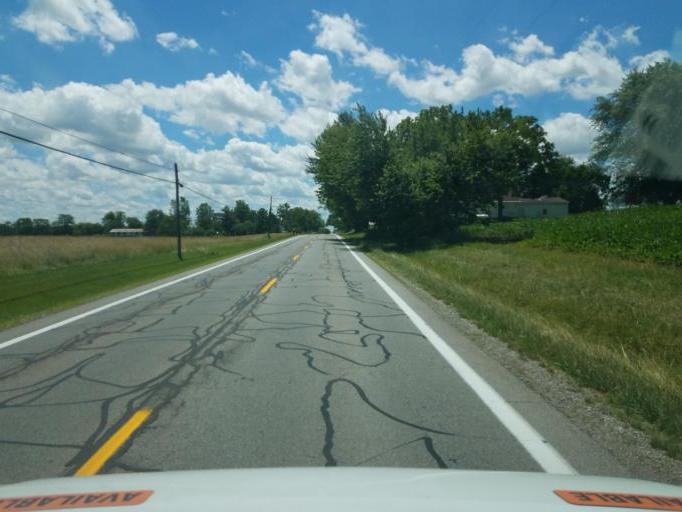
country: US
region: Ohio
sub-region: Morrow County
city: Mount Gilead
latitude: 40.5910
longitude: -82.8239
